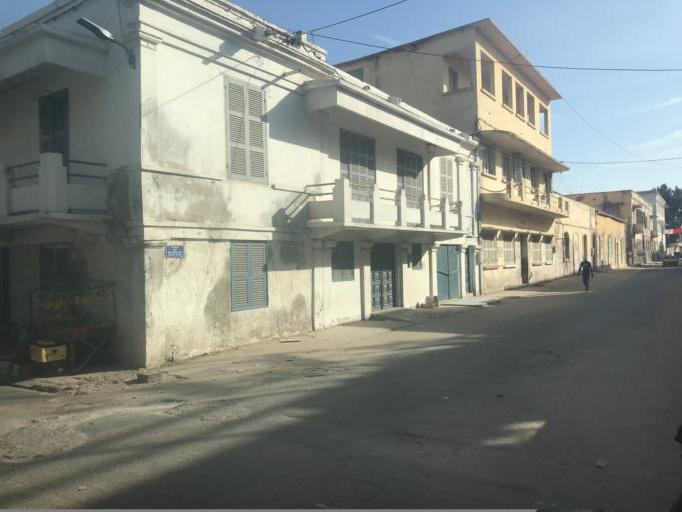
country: SN
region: Saint-Louis
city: Saint-Louis
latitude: 16.0248
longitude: -16.5043
